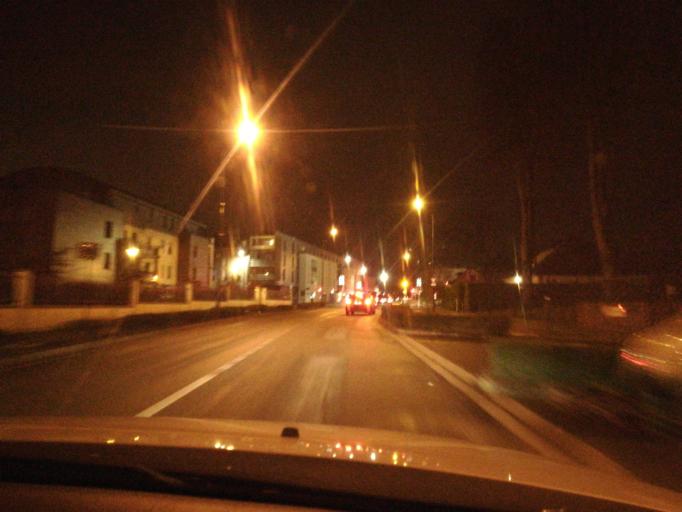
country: FR
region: Haute-Normandie
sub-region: Departement de la Seine-Maritime
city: Bois-Guillaume
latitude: 49.4696
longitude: 1.1226
